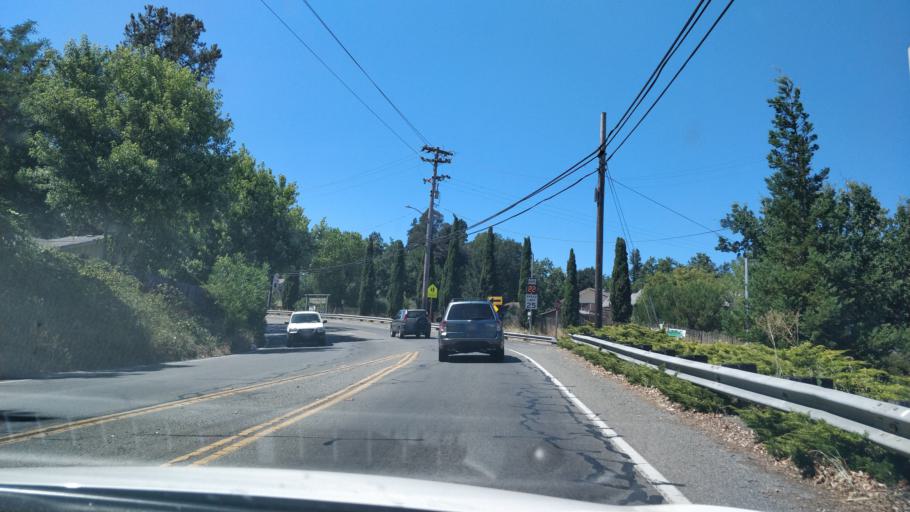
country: US
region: California
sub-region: Sonoma County
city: Forestville
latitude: 38.4732
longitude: -122.8885
